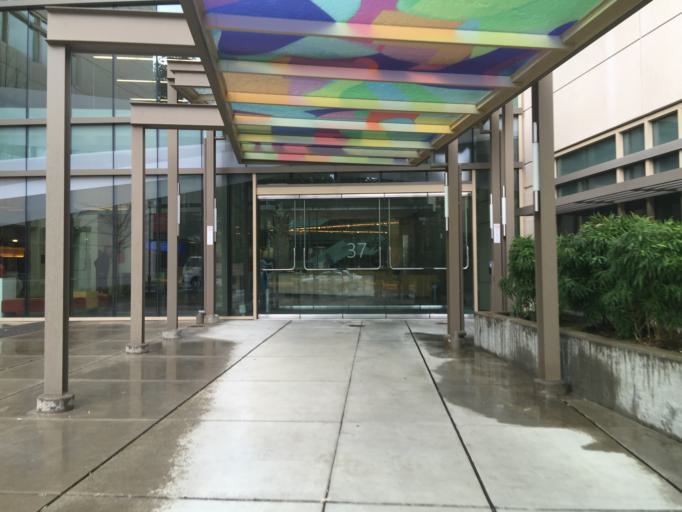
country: US
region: Washington
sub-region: King County
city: Redmond
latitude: 47.6383
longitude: -122.1254
